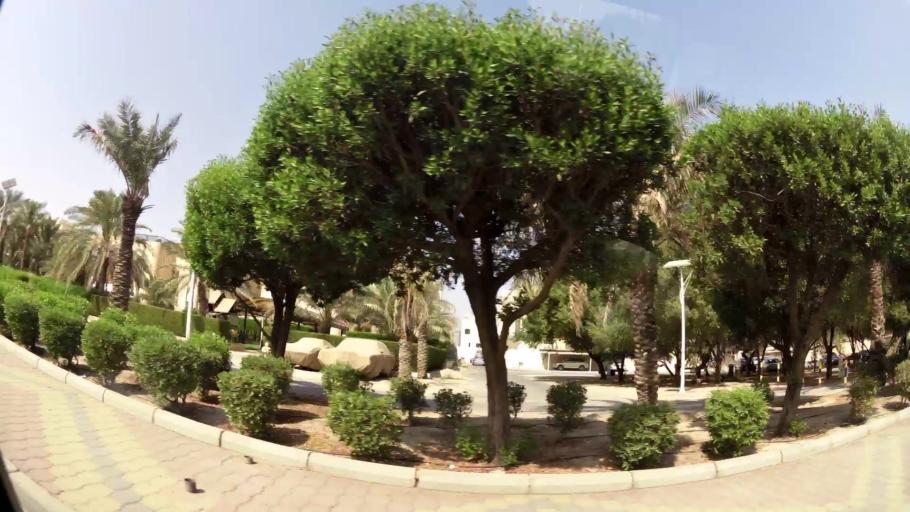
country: KW
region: Al Asimah
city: Ad Dasmah
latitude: 29.3376
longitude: 47.9945
